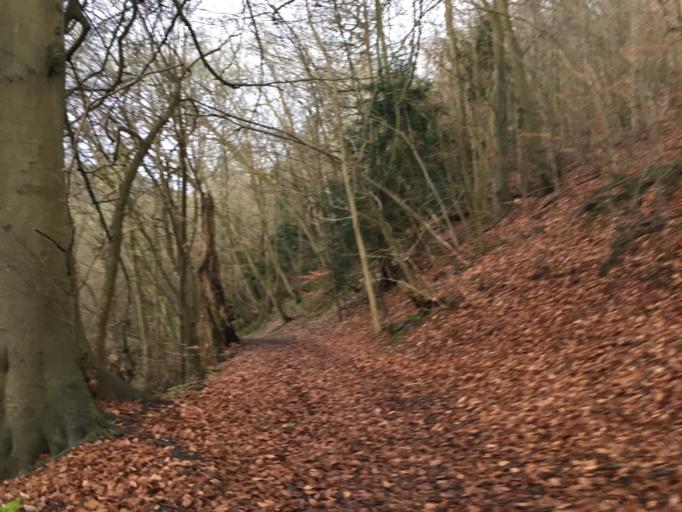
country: GB
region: England
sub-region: Surrey
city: Mickleham
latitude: 51.2602
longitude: -0.3377
